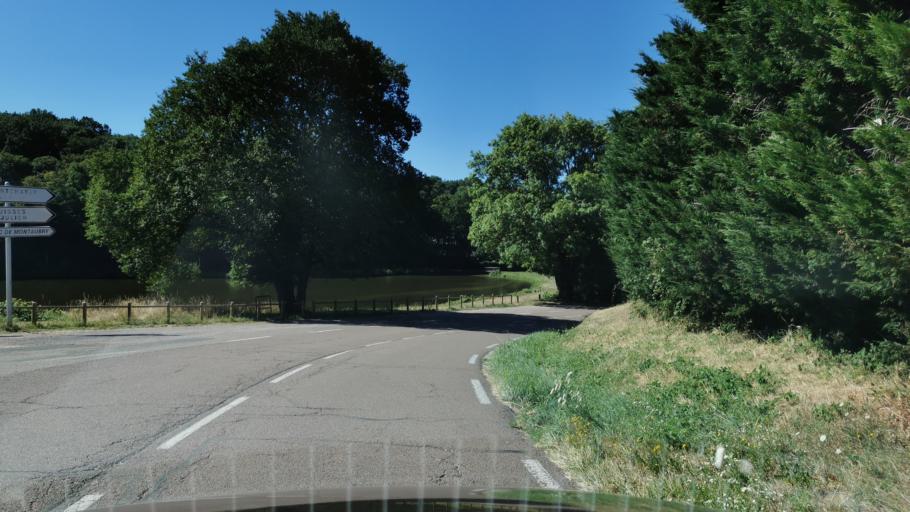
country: FR
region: Bourgogne
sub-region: Departement de Saone-et-Loire
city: Le Breuil
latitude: 46.7941
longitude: 4.4844
